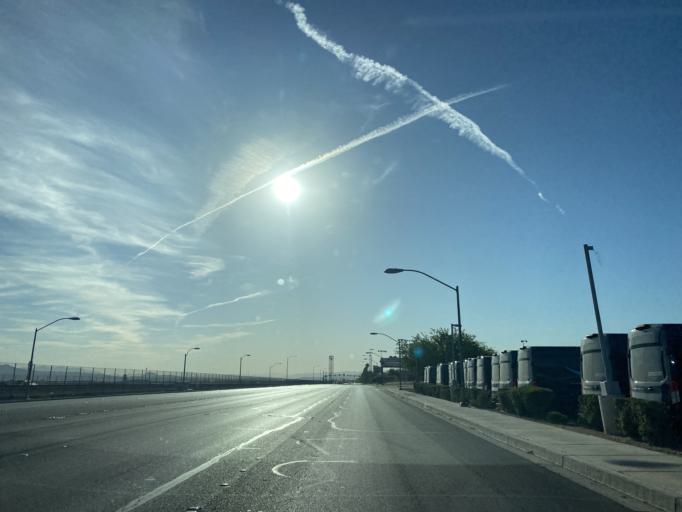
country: US
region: Nevada
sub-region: Clark County
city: Paradise
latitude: 36.0711
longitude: -115.1680
